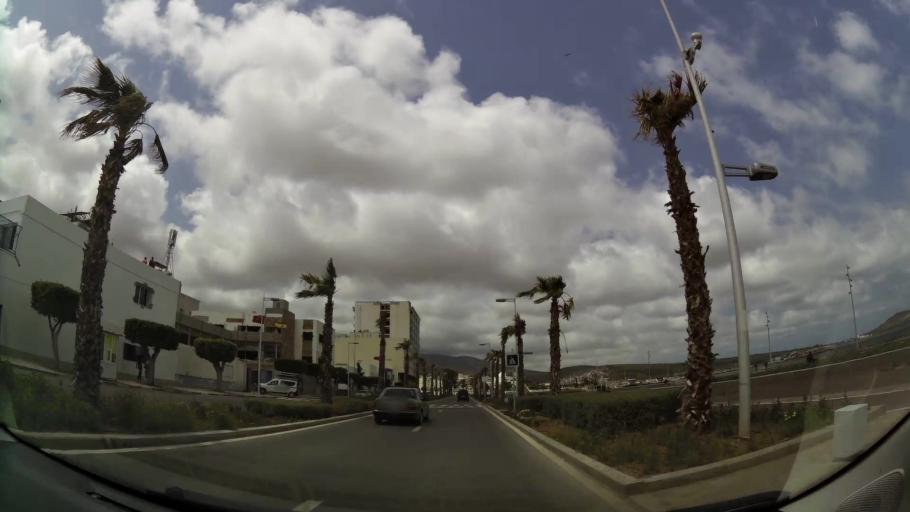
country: MA
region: Oriental
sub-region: Nador
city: Nador
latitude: 35.1829
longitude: -2.9241
